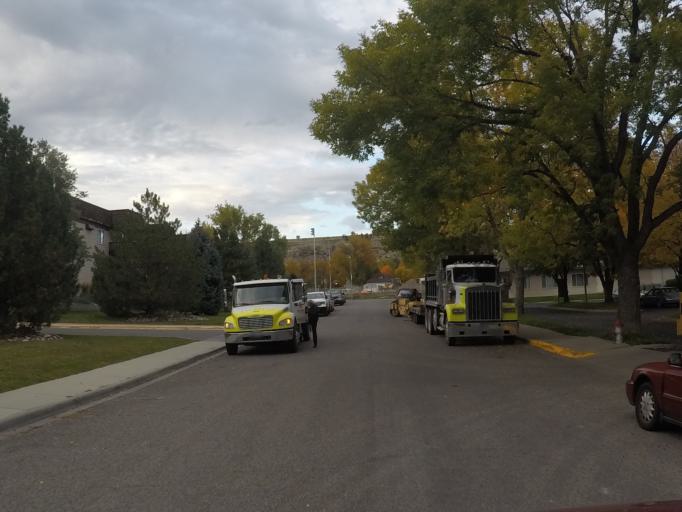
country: US
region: Montana
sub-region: Yellowstone County
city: Billings
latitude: 45.7940
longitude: -108.5556
